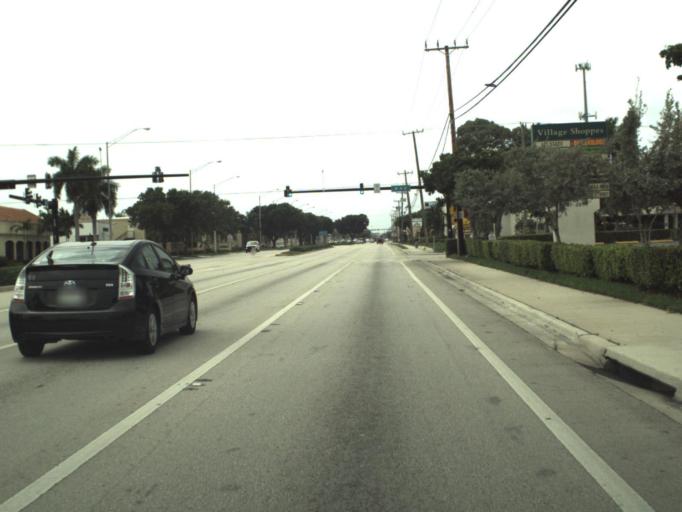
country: US
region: Florida
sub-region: Broward County
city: Pompano Beach Highlands
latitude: 26.2800
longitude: -80.0969
